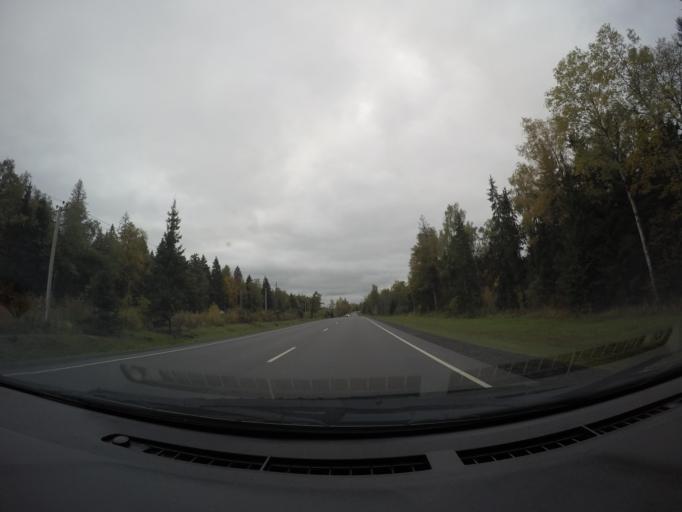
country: RU
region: Moskovskaya
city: Ruza
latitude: 55.7219
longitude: 36.2137
